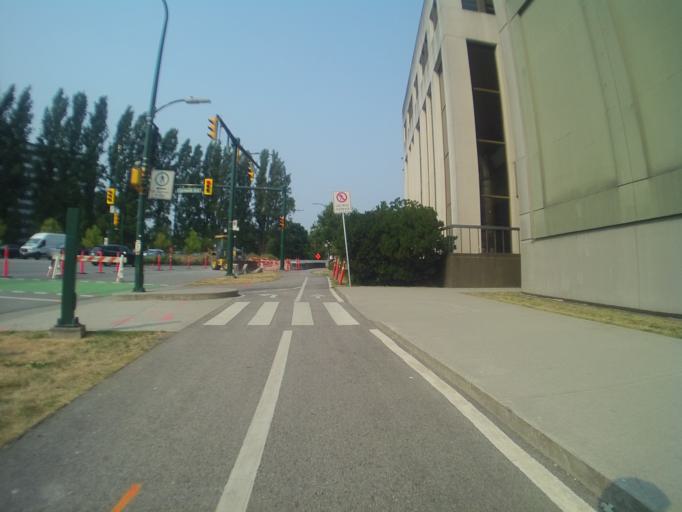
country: CA
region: British Columbia
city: West End
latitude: 49.2722
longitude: -123.1451
